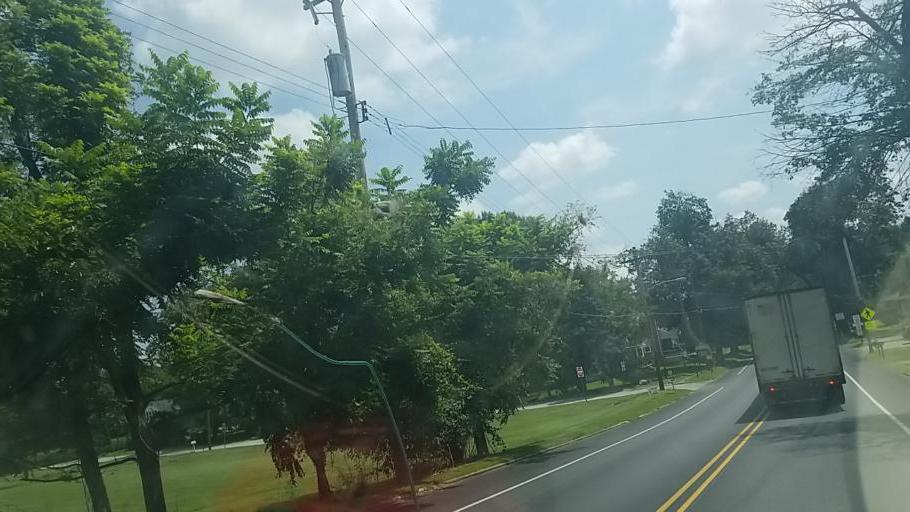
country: US
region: Pennsylvania
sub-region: Chester County
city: Avondale
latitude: 39.8301
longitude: -75.7864
